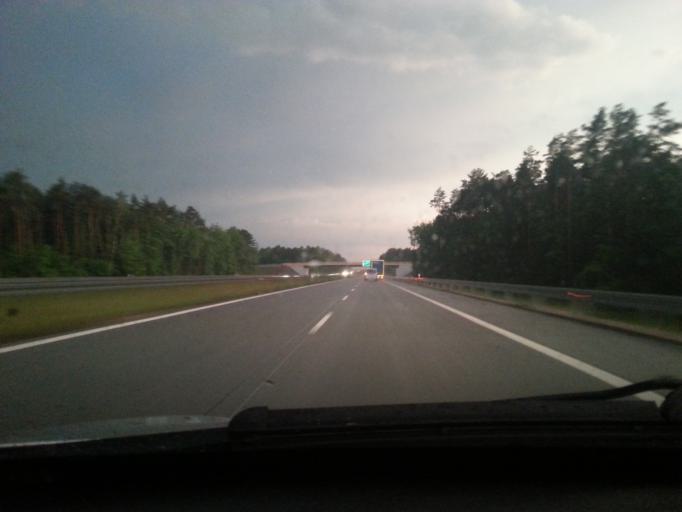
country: PL
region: Lodz Voivodeship
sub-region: Powiat laski
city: Lask
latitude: 51.5821
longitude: 19.1928
